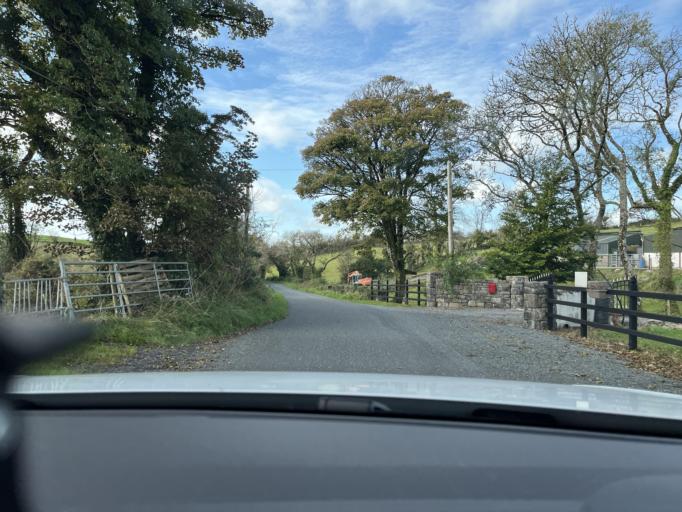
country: IE
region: Connaught
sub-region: Sligo
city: Ballymote
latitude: 54.0767
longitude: -8.4402
